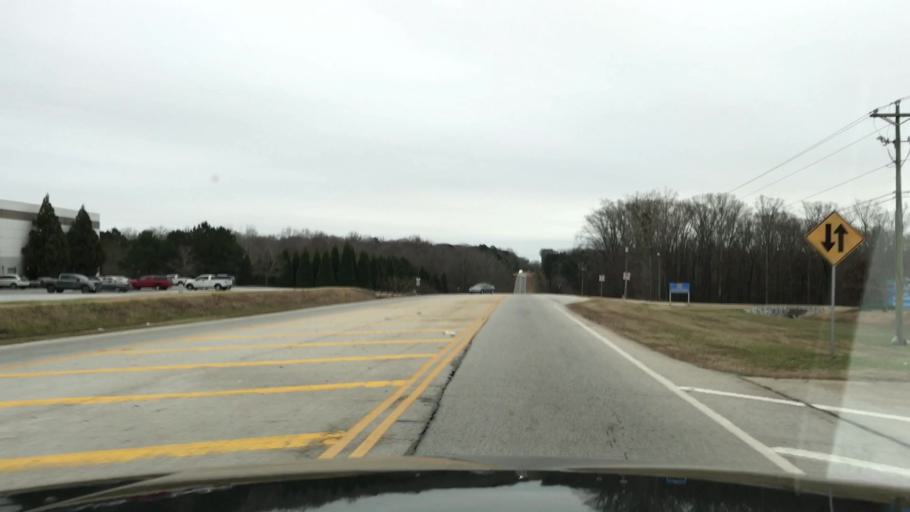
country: US
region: Georgia
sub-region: Walton County
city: Monroe
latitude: 33.8073
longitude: -83.6757
